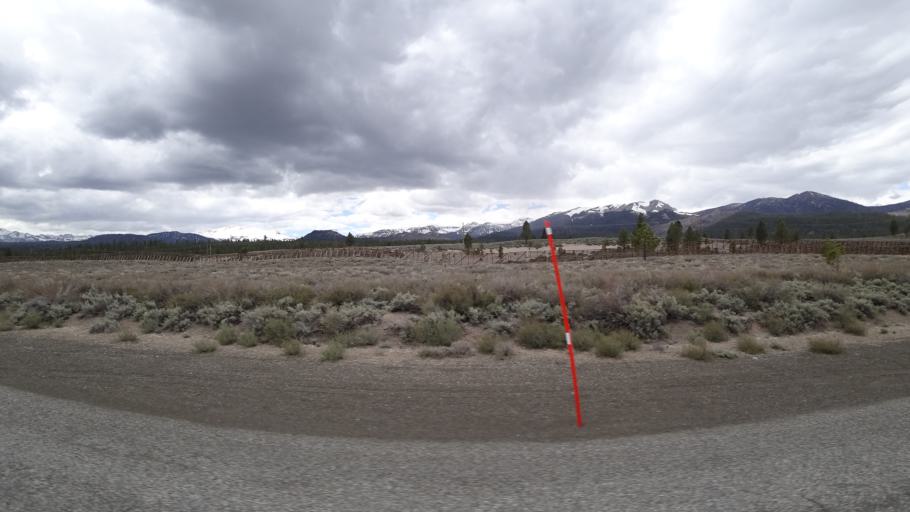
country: US
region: California
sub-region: Mono County
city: Mammoth Lakes
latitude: 37.7398
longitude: -118.9744
